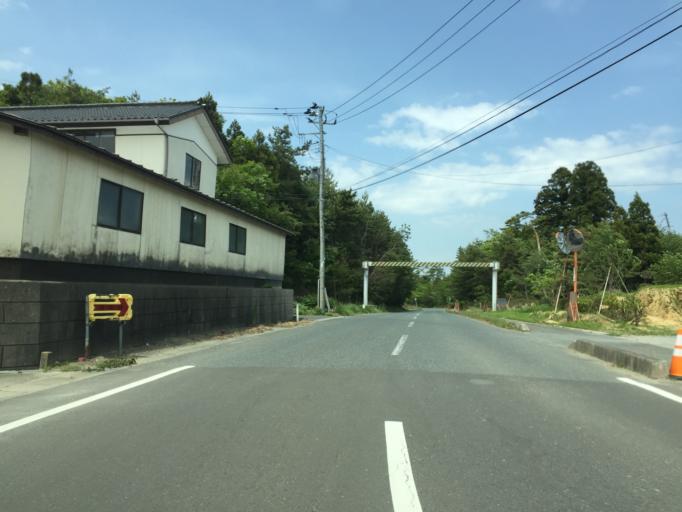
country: JP
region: Miyagi
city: Marumori
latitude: 37.8540
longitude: 140.9455
